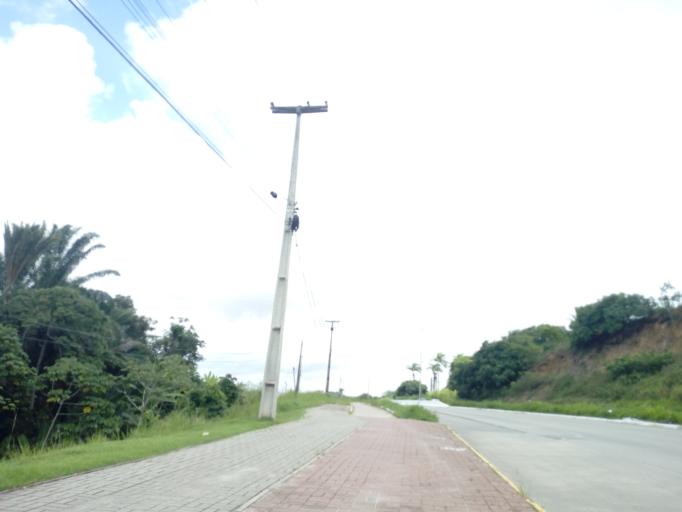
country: BR
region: Pernambuco
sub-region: Cabo De Santo Agostinho
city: Cabo
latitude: -8.2657
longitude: -35.0184
